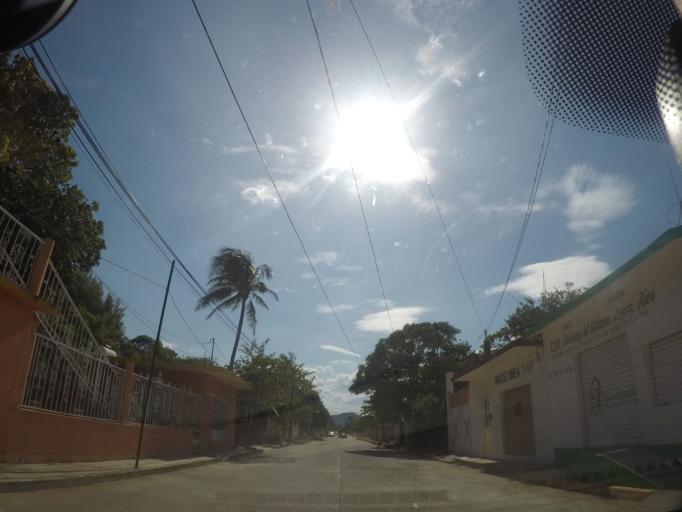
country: MX
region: Oaxaca
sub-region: Salina Cruz
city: Salina Cruz
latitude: 16.2144
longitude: -95.1966
